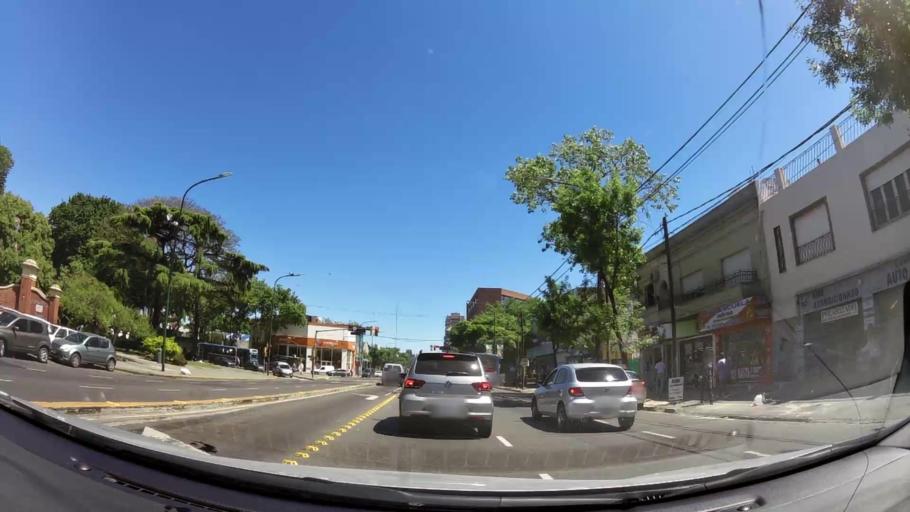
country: AR
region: Buenos Aires
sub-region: Partido de San Isidro
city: San Isidro
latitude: -34.4747
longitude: -58.5121
